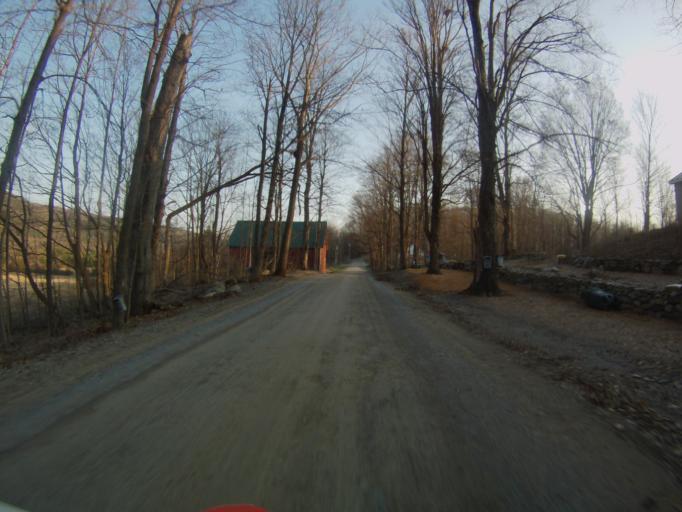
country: US
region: Vermont
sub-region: Addison County
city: Middlebury (village)
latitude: 44.0489
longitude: -73.1034
